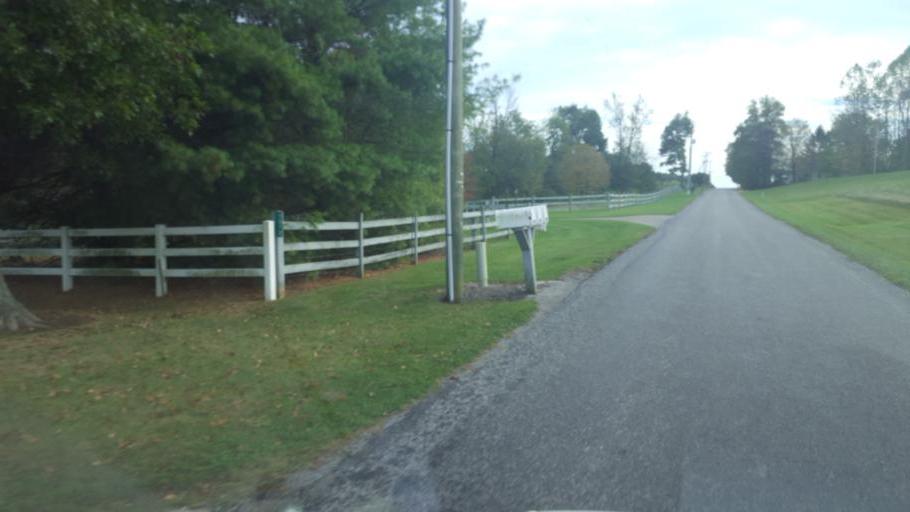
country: US
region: Ohio
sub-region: Holmes County
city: Millersburg
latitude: 40.5715
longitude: -81.8398
